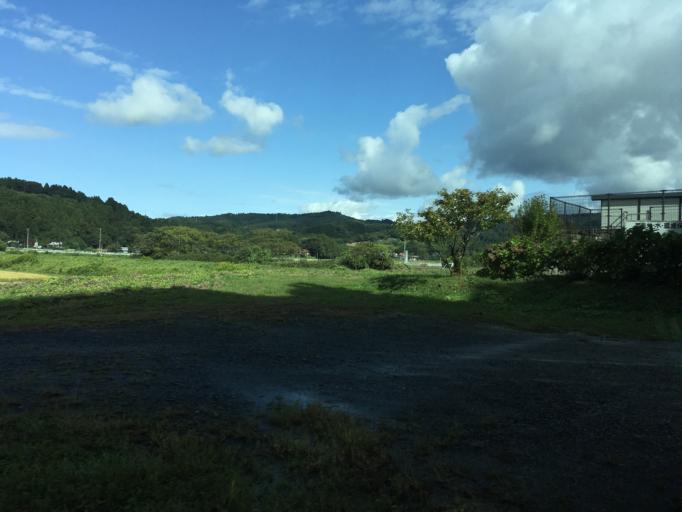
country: JP
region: Iwate
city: Ichinoseki
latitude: 38.8492
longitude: 141.2824
